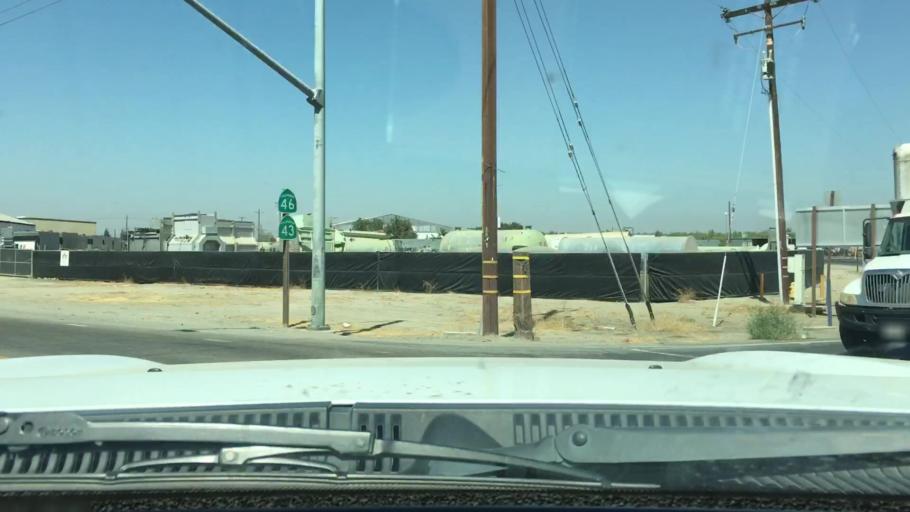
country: US
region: California
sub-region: Kern County
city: Wasco
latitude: 35.6013
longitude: -119.3281
